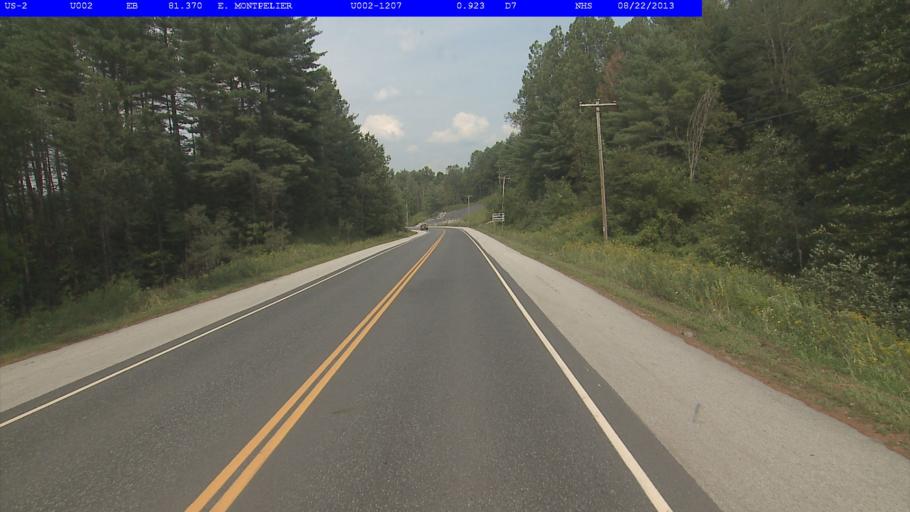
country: US
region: Vermont
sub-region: Washington County
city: Barre
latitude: 44.2467
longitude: -72.5023
